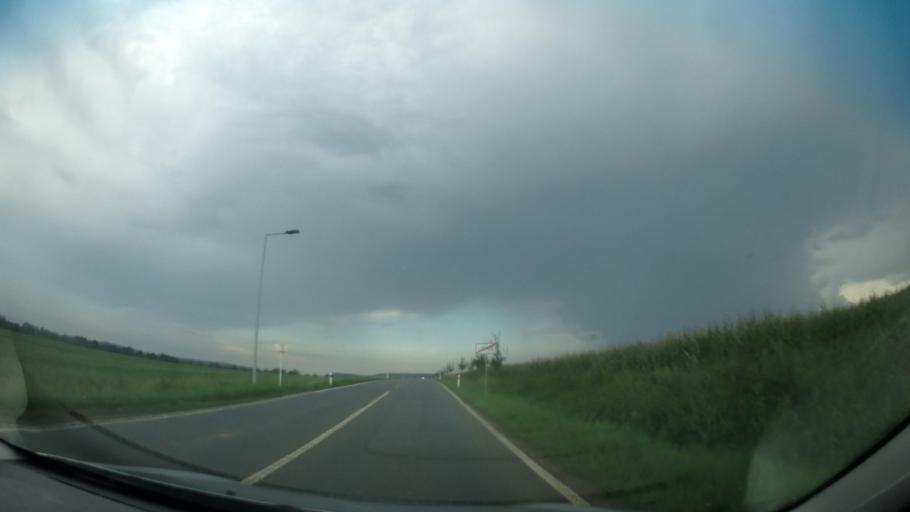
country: CZ
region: Olomoucky
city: Lostice
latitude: 49.7398
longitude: 16.9449
